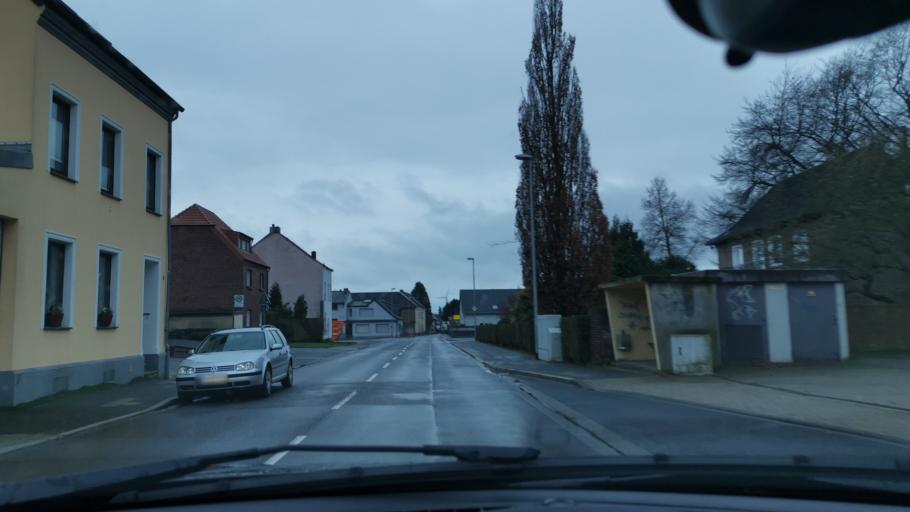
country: DE
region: North Rhine-Westphalia
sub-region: Regierungsbezirk Koln
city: Titz
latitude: 51.0015
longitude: 6.4875
